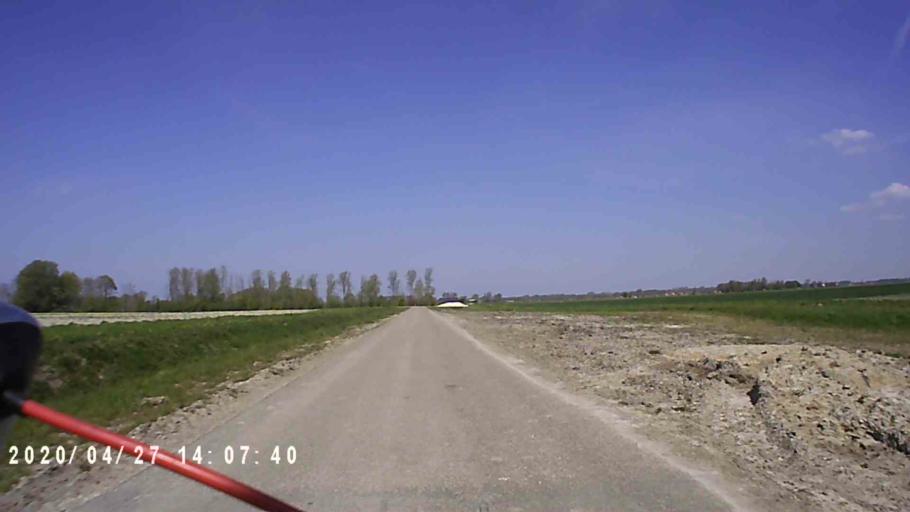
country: NL
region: Groningen
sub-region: Gemeente Zuidhorn
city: Oldehove
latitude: 53.3439
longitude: 6.3941
